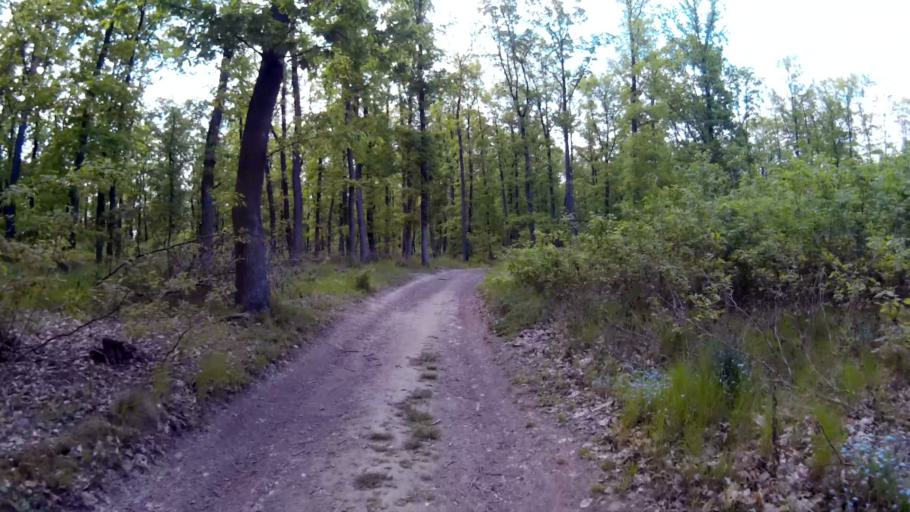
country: CZ
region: South Moravian
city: Troubsko
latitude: 49.1884
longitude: 16.5181
